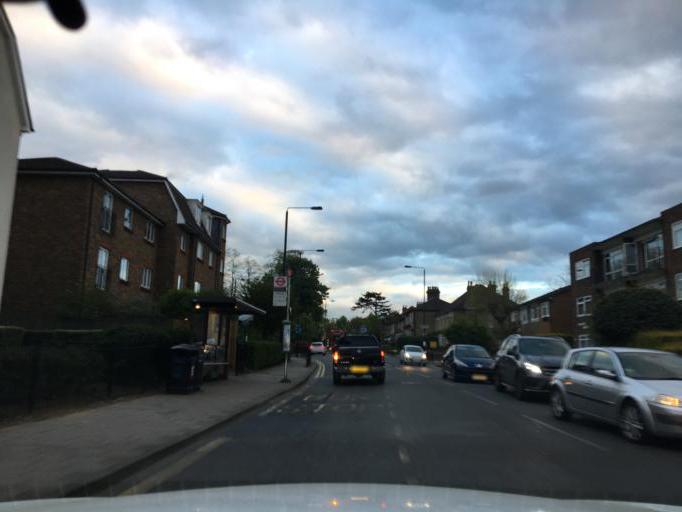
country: GB
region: England
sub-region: Greater London
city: Sidcup
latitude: 51.4257
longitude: 0.1009
